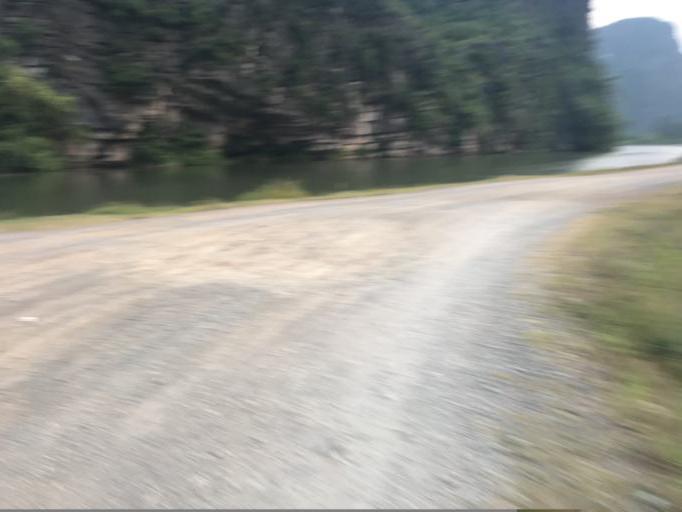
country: VN
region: Ninh Binh
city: Thi Tran Thien Ton
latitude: 20.2553
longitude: 105.9285
